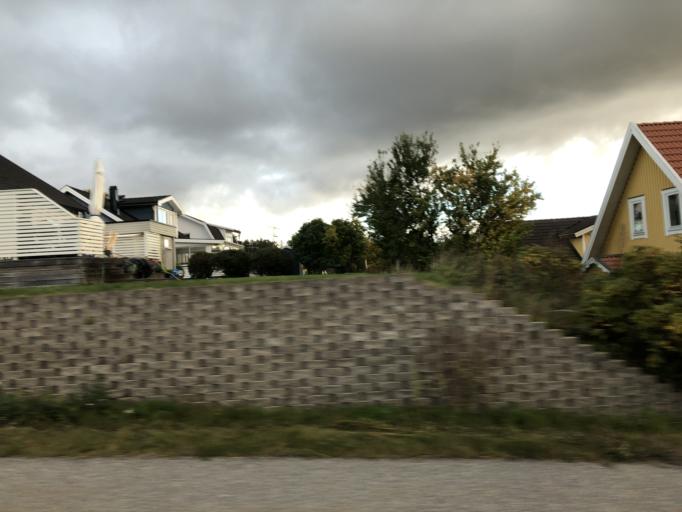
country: SE
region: Stockholm
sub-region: Jarfalla Kommun
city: Jakobsberg
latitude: 59.4249
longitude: 17.8095
